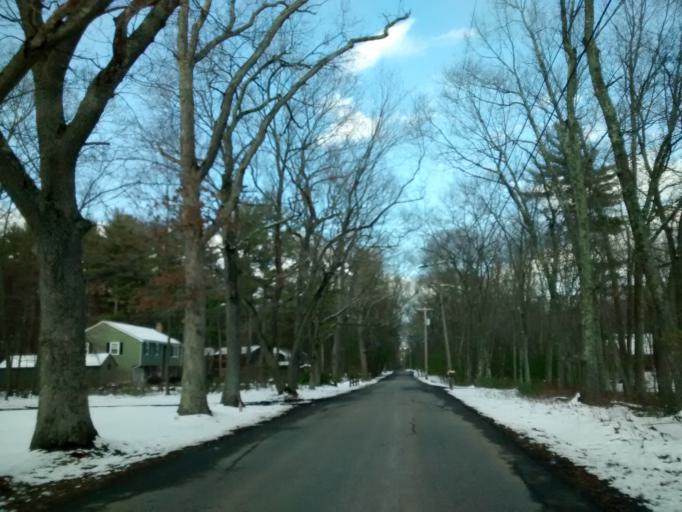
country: US
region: Massachusetts
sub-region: Worcester County
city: Uxbridge
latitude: 42.0298
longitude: -71.6673
